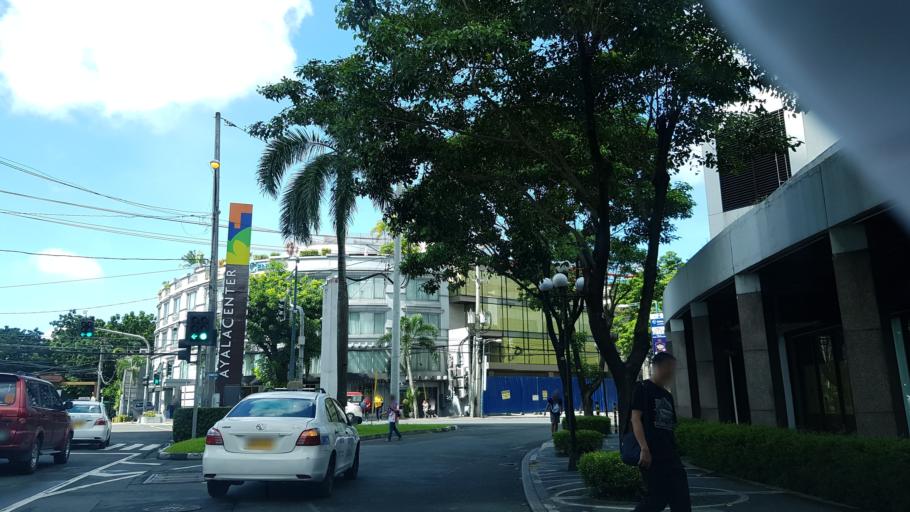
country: PH
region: Metro Manila
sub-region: Makati City
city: Makati City
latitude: 14.5510
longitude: 121.0225
